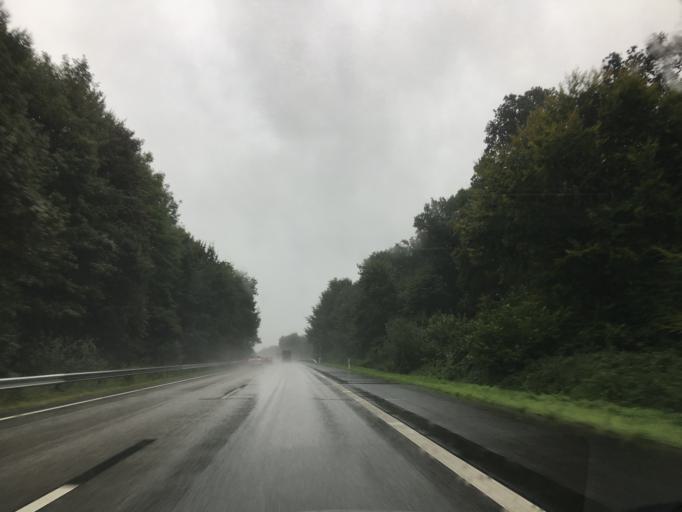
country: DE
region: Schleswig-Holstein
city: Schonbek
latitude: 54.1804
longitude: 9.9574
